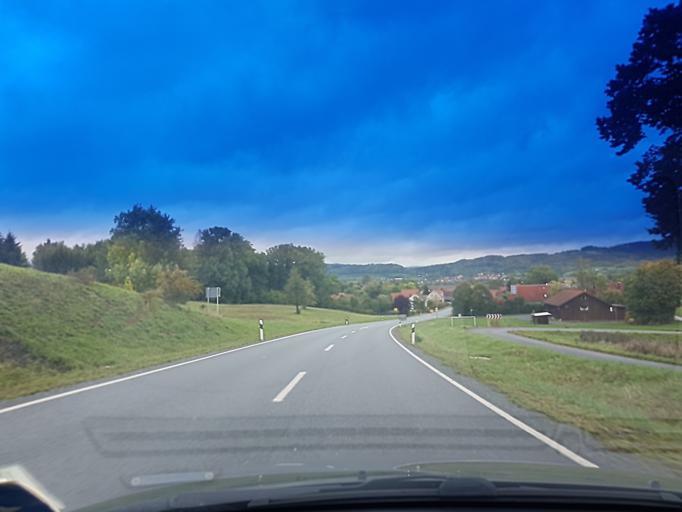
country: DE
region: Bavaria
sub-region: Upper Franconia
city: Goldkronach
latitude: 49.9920
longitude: 11.6563
